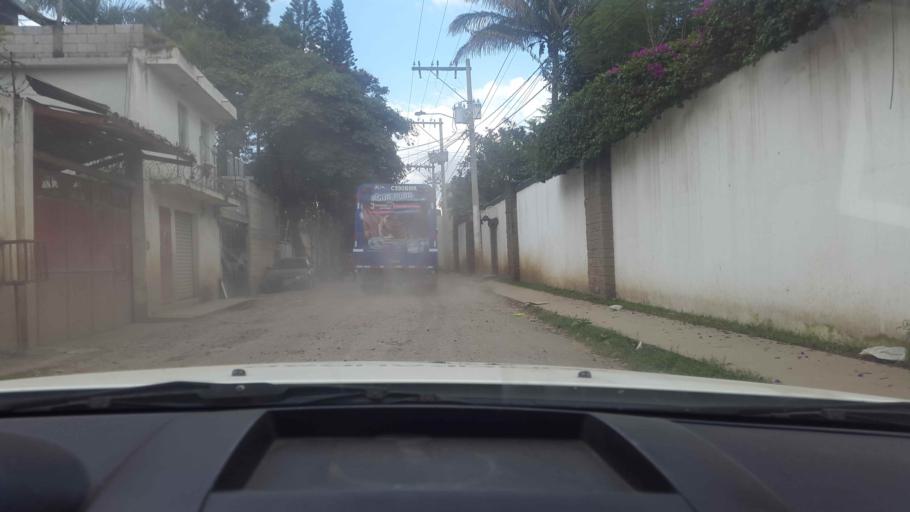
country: GT
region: Guatemala
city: Petapa
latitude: 14.5205
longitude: -90.5363
